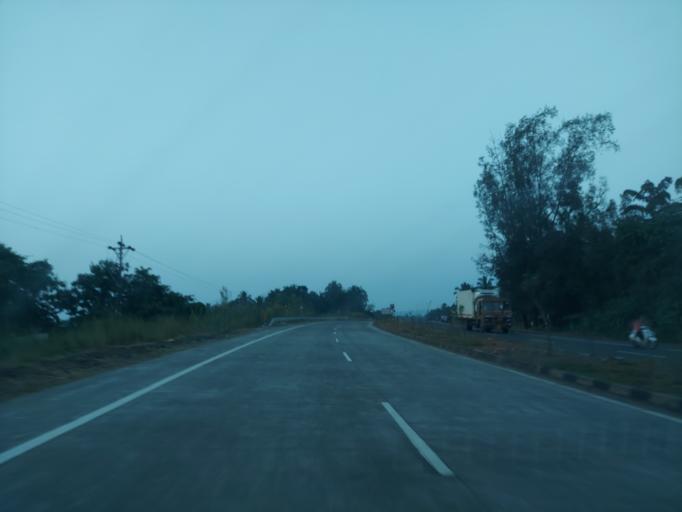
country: IN
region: Maharashtra
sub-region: Sindhudurg
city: Kudal
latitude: 16.0933
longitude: 73.7061
